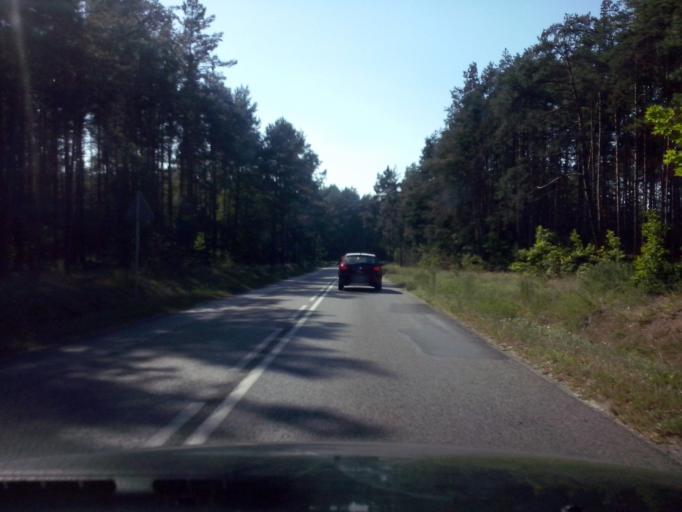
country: PL
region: Swietokrzyskie
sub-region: Powiat kielecki
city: Daleszyce
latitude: 50.8124
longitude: 20.7303
